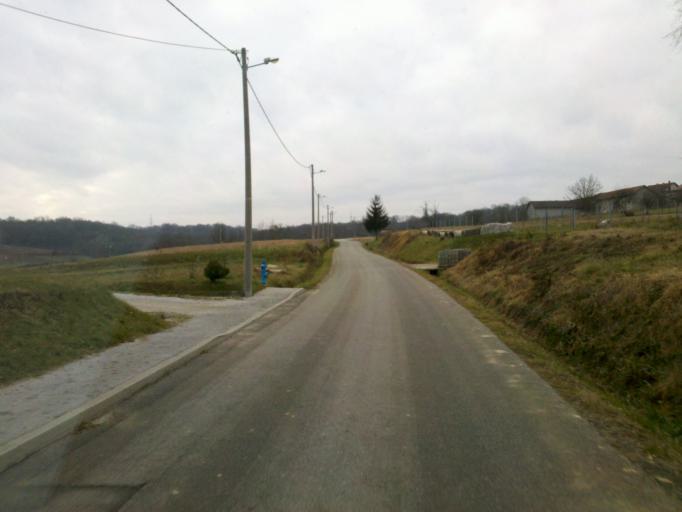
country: HR
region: Grad Zagreb
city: Horvati
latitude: 45.6857
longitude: 15.8480
